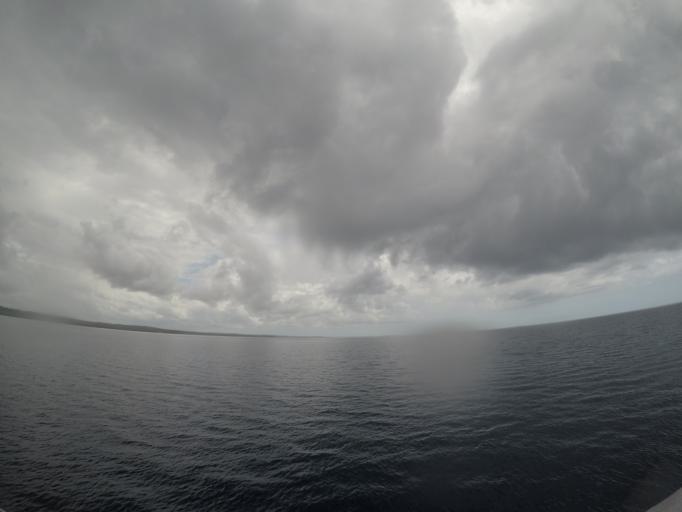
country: TZ
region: Zanzibar North
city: Mkokotoni
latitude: -6.0077
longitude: 39.1786
